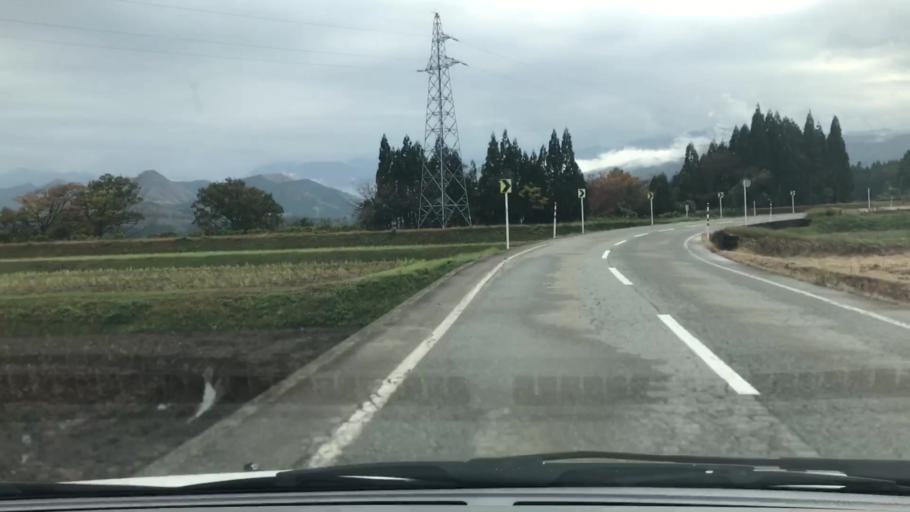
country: JP
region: Toyama
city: Kamiichi
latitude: 36.5994
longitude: 137.3121
